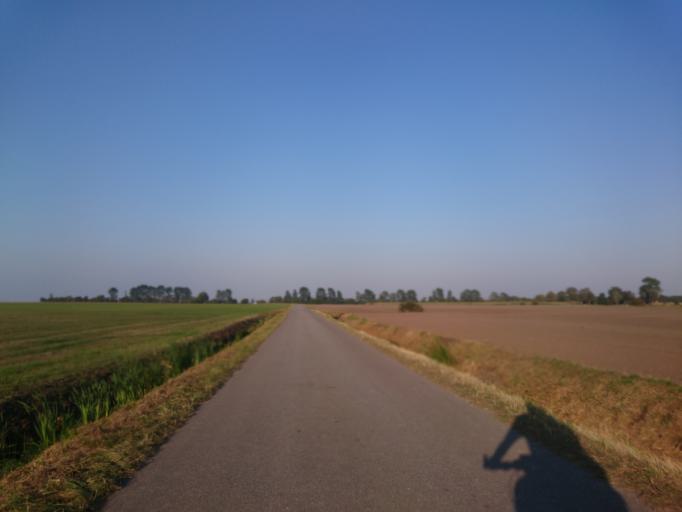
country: DE
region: Mecklenburg-Vorpommern
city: Velgast
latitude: 54.3386
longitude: 12.8162
